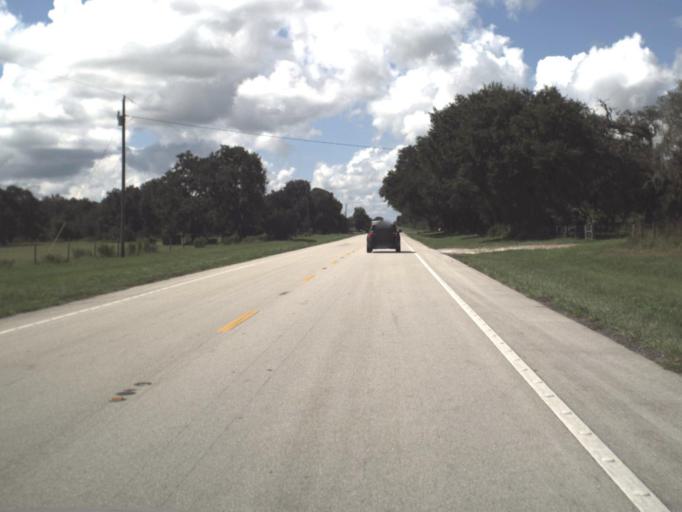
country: US
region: Florida
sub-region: DeSoto County
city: Arcadia
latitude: 27.2750
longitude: -82.0151
